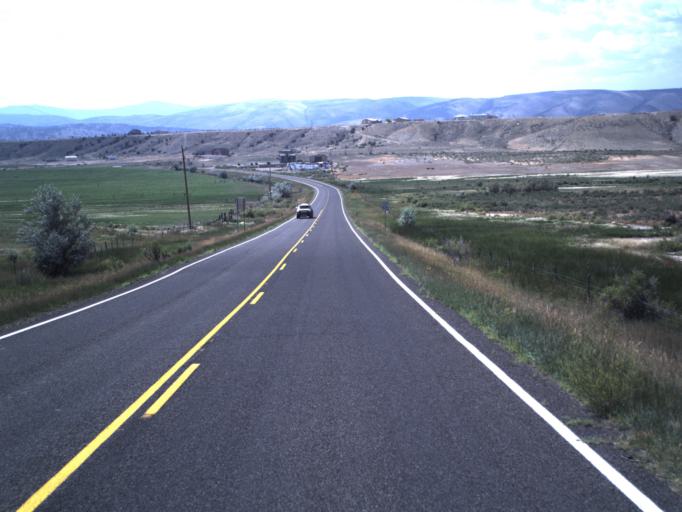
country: US
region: Utah
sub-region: Daggett County
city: Manila
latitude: 40.9807
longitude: -109.7227
